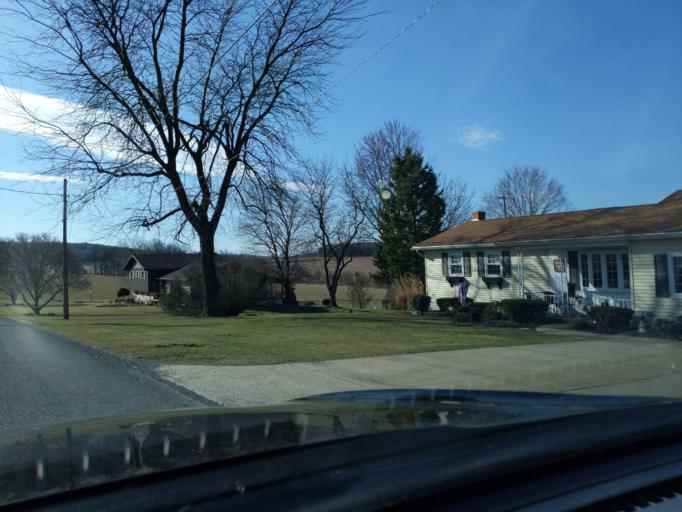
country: US
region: Pennsylvania
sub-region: Blair County
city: Martinsburg
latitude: 40.3966
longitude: -78.2760
